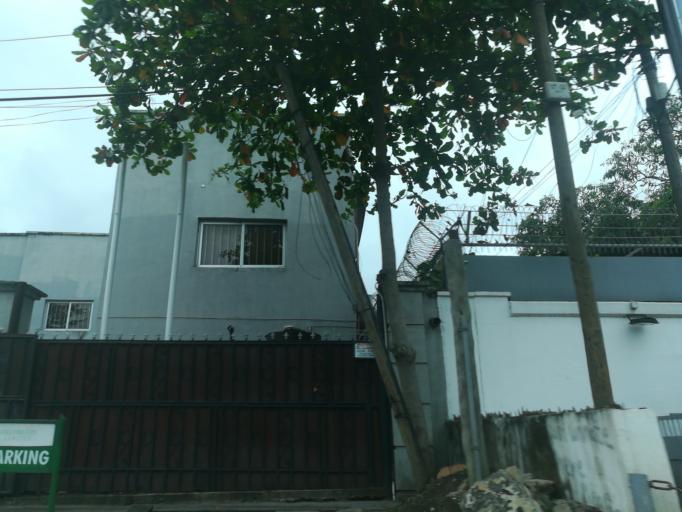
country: NG
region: Lagos
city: Ikoyi
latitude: 6.4355
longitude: 3.4173
